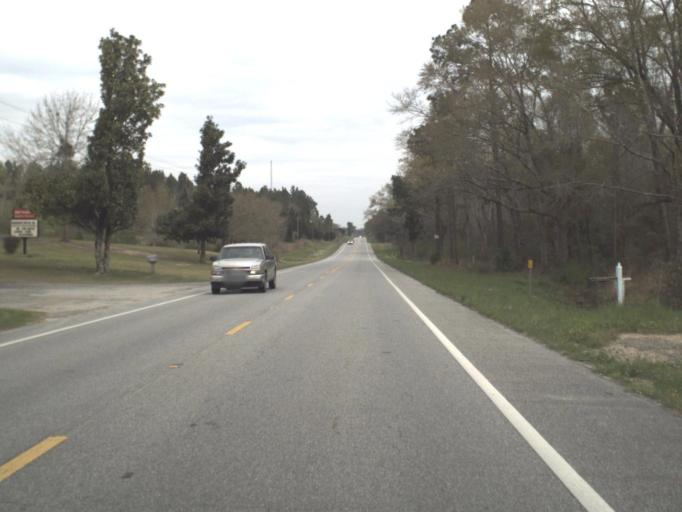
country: US
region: Florida
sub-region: Jackson County
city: Graceville
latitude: 30.9321
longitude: -85.6491
